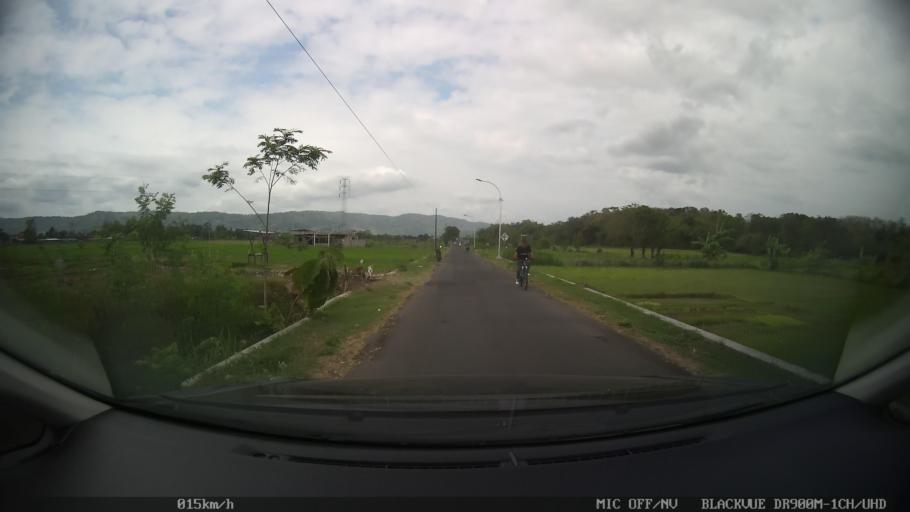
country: ID
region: Daerah Istimewa Yogyakarta
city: Depok
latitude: -7.8121
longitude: 110.4655
